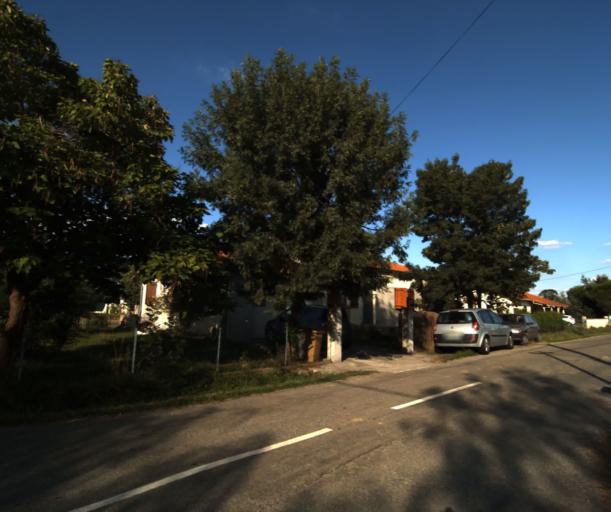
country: FR
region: Midi-Pyrenees
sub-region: Departement de la Haute-Garonne
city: Labastidette
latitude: 43.4546
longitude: 1.2446
